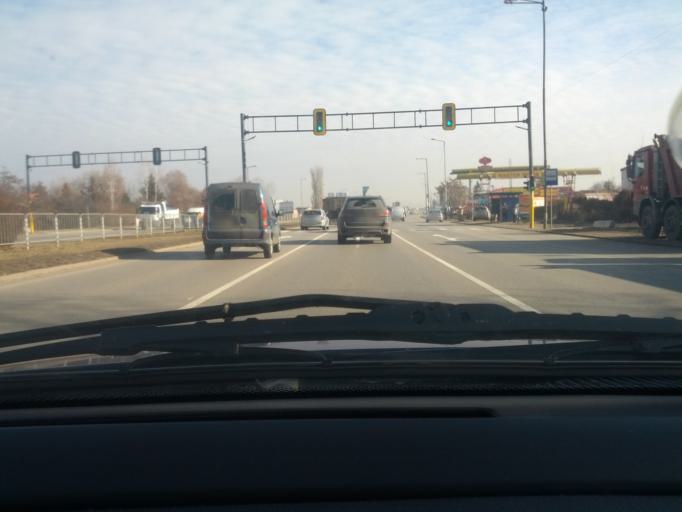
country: BG
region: Sofia-Capital
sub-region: Stolichna Obshtina
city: Sofia
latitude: 42.7093
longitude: 23.4238
